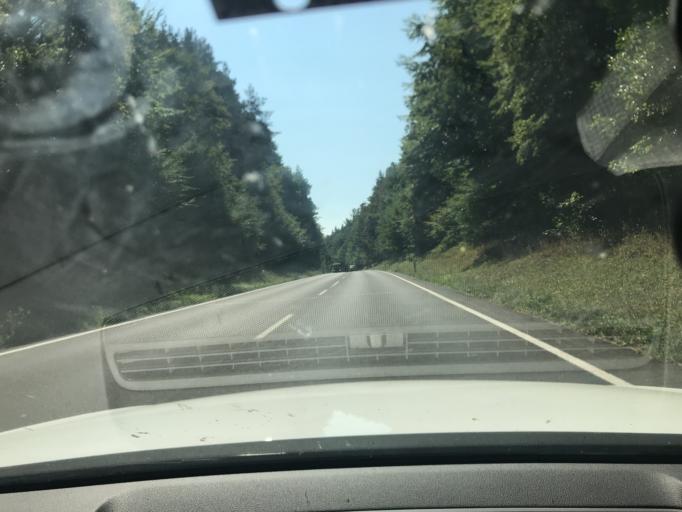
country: DE
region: Bavaria
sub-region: Upper Palatinate
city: Sulzbach-Rosenberg
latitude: 49.4816
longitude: 11.7339
